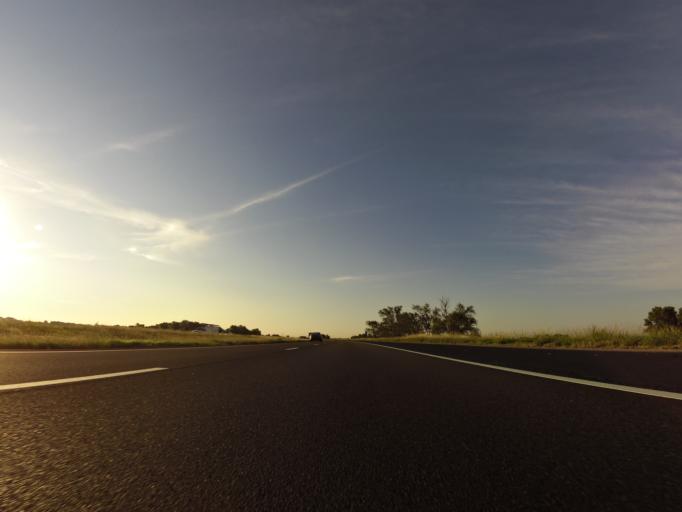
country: US
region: Kansas
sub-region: Sedgwick County
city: Maize
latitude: 37.8044
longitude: -97.4961
